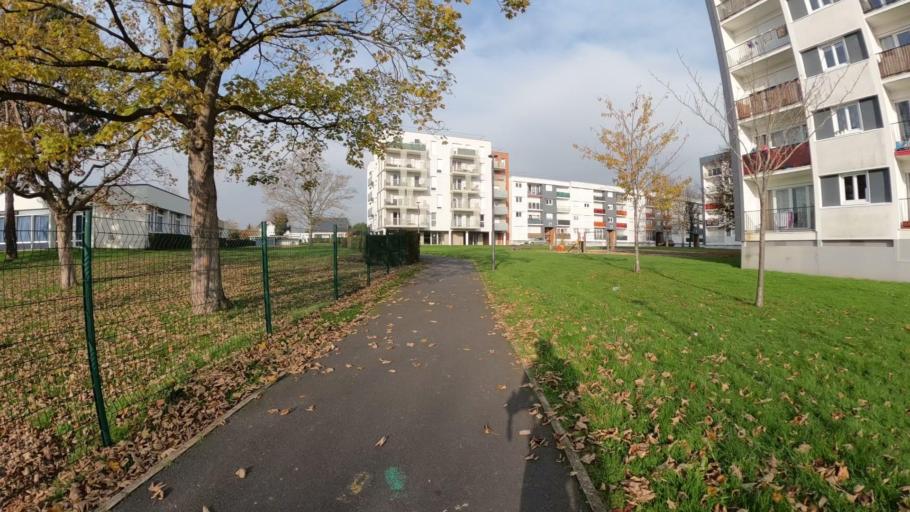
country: FR
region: Lower Normandy
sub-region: Departement du Calvados
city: Saint-Germain-la-Blanche-Herbe
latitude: 49.1897
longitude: -0.4106
